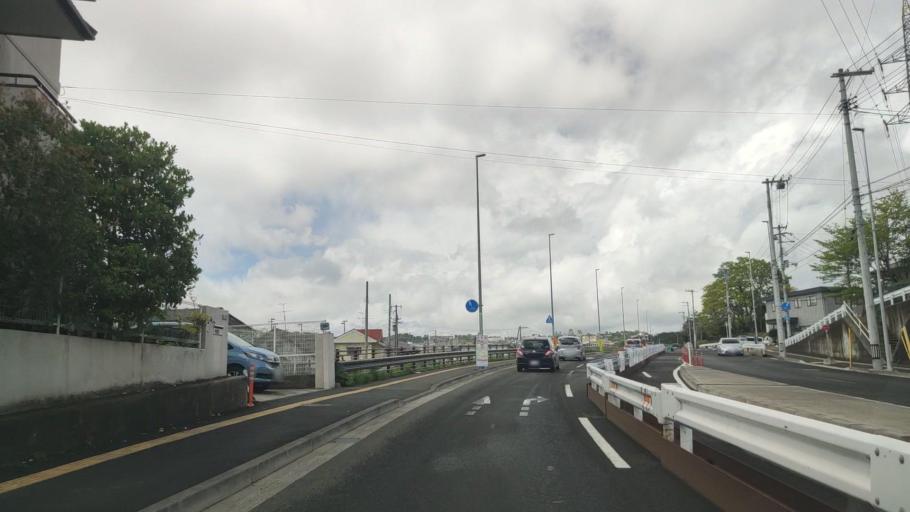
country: JP
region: Miyagi
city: Sendai
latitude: 38.2271
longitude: 140.8589
